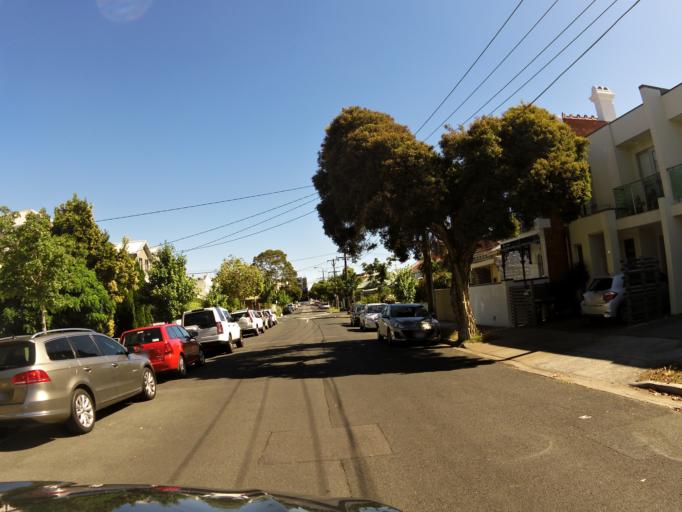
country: AU
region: Victoria
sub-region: Yarra
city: Richmond
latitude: -37.8241
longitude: 145.0059
